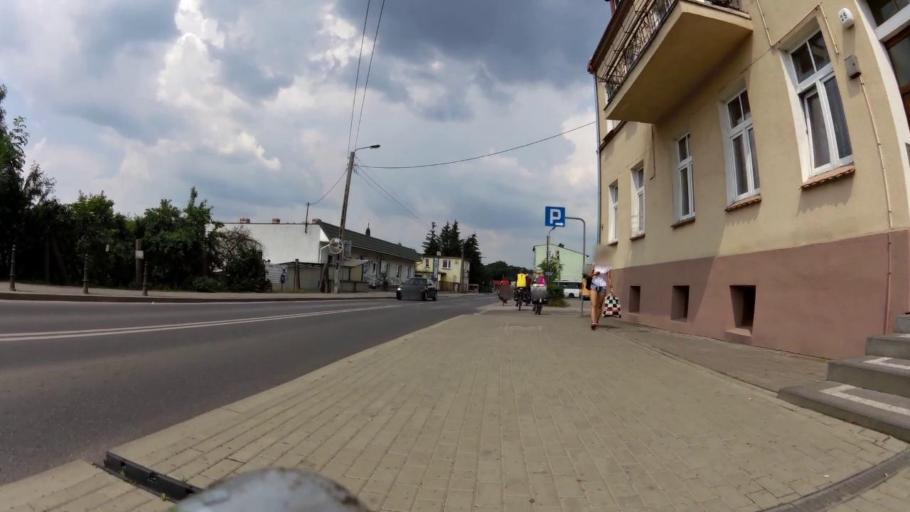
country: PL
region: Kujawsko-Pomorskie
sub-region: Powiat bydgoski
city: Koronowo
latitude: 53.3117
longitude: 17.9391
